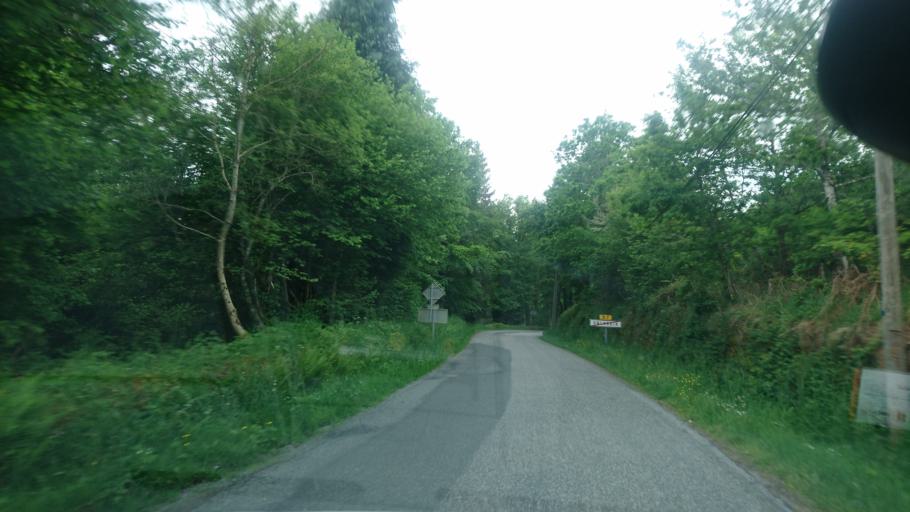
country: FR
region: Limousin
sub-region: Departement de la Haute-Vienne
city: Peyrat-le-Chateau
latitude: 45.8314
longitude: 1.8797
